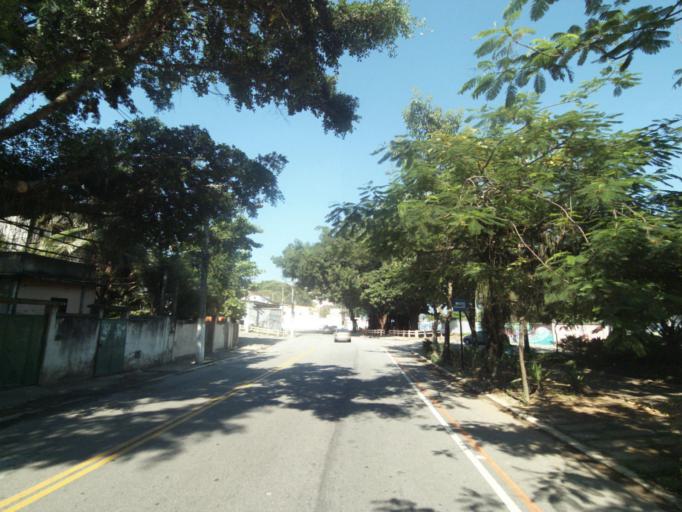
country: BR
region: Rio de Janeiro
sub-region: Niteroi
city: Niteroi
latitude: -22.9020
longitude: -43.1347
